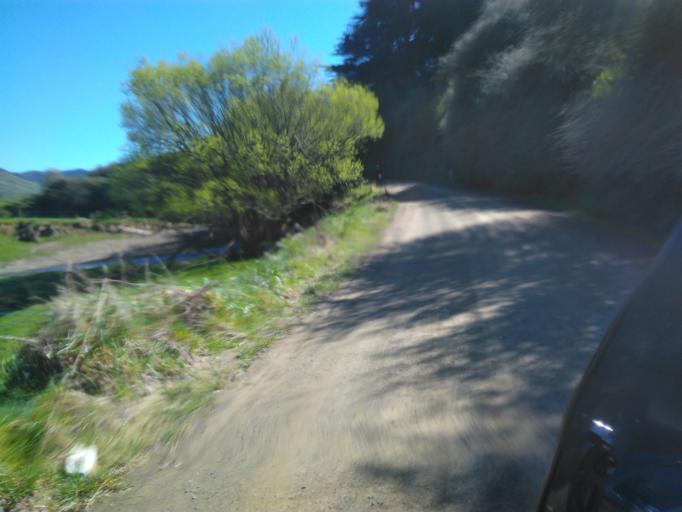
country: NZ
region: Bay of Plenty
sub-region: Opotiki District
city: Opotiki
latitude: -38.2899
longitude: 177.5454
